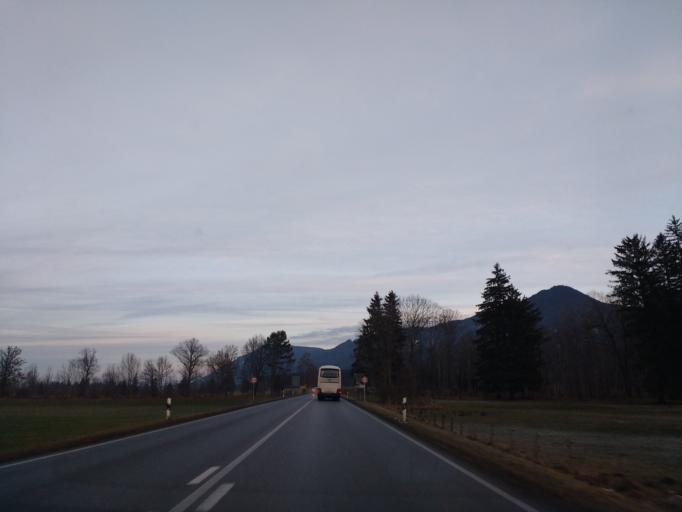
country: DE
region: Bavaria
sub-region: Swabia
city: Schwangau
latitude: 47.5830
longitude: 10.7550
